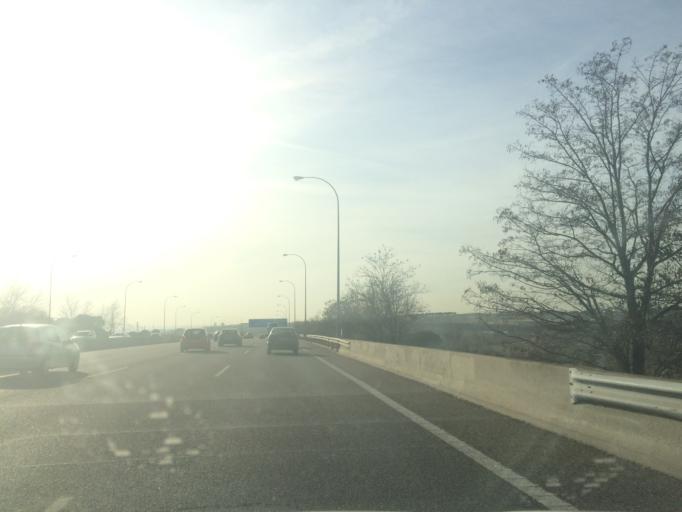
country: ES
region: Madrid
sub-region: Provincia de Madrid
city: Fuencarral-El Pardo
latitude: 40.5069
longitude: -3.7104
